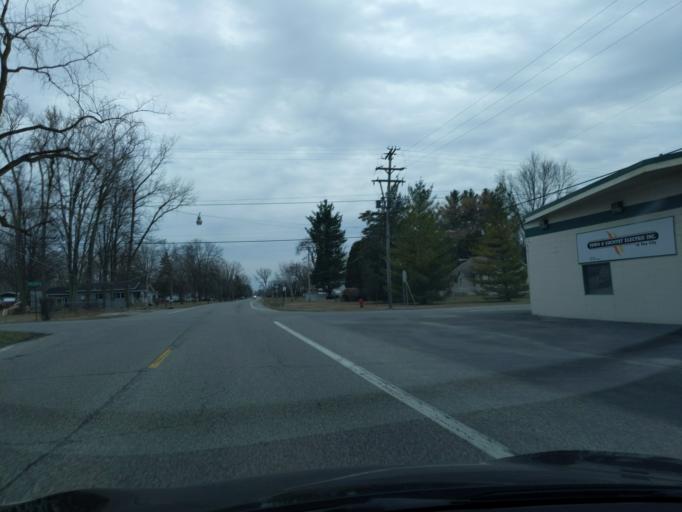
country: US
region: Michigan
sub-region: Bay County
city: Bay City
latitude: 43.6532
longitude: -83.9125
